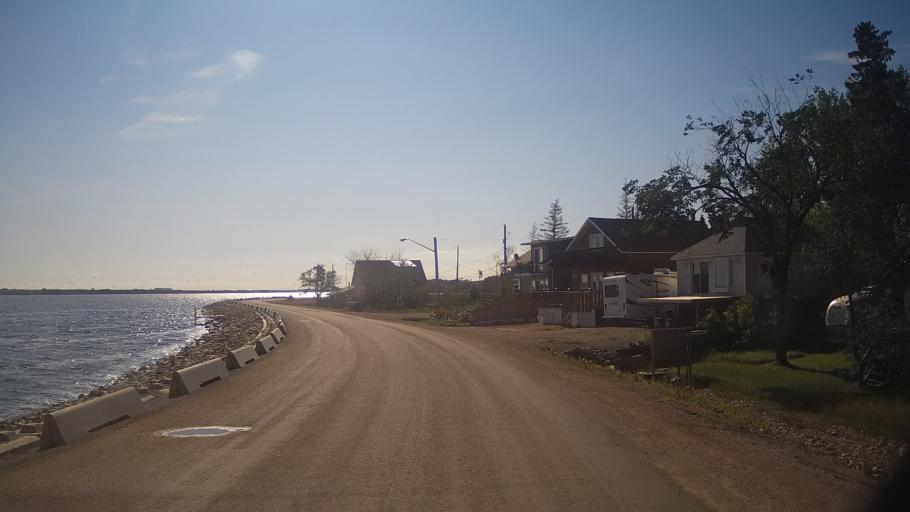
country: CA
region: Saskatchewan
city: Watrous
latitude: 51.7187
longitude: -105.4279
